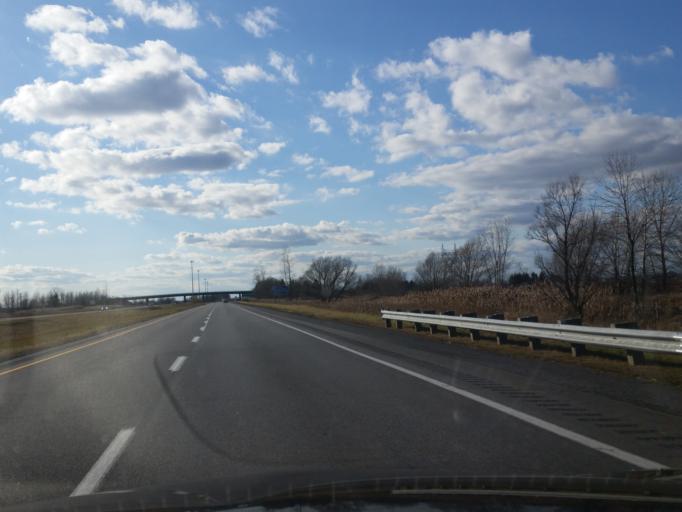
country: CA
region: Quebec
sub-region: Mauricie
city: Maskinonge
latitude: 46.1642
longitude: -73.0785
